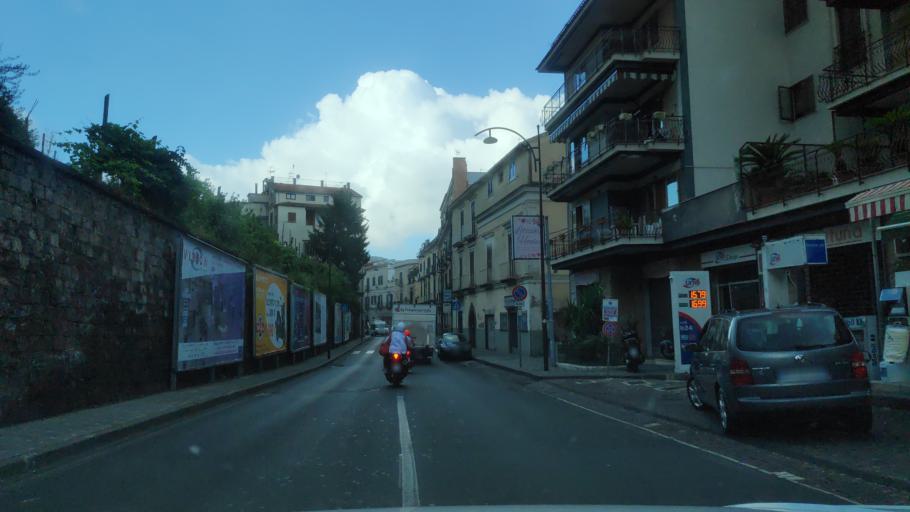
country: IT
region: Campania
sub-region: Provincia di Napoli
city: Meta
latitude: 40.6396
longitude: 14.4189
